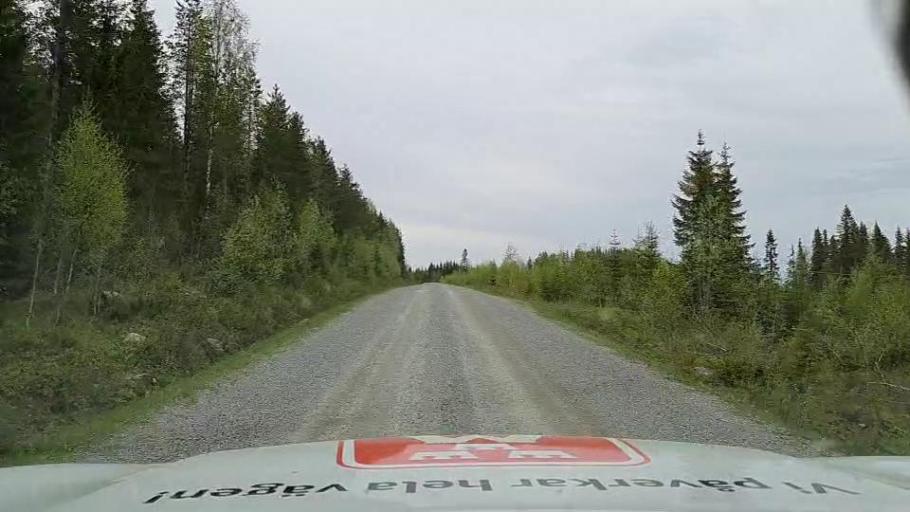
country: SE
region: Jaemtland
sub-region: OEstersunds Kommun
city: Brunflo
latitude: 62.6288
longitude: 14.9414
